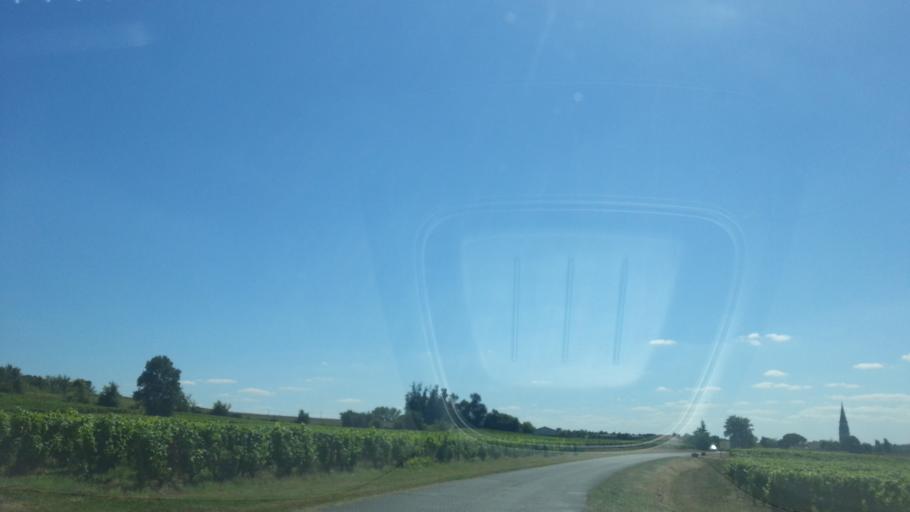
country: FR
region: Aquitaine
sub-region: Departement de la Gironde
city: Illats
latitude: 44.5493
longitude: -0.3524
